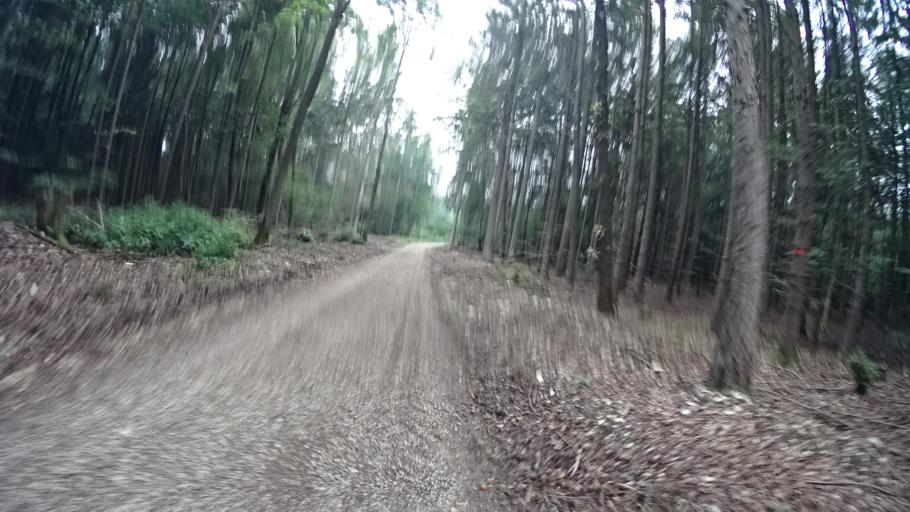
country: DE
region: Bavaria
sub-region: Upper Bavaria
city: Stammham
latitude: 48.8447
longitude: 11.4821
